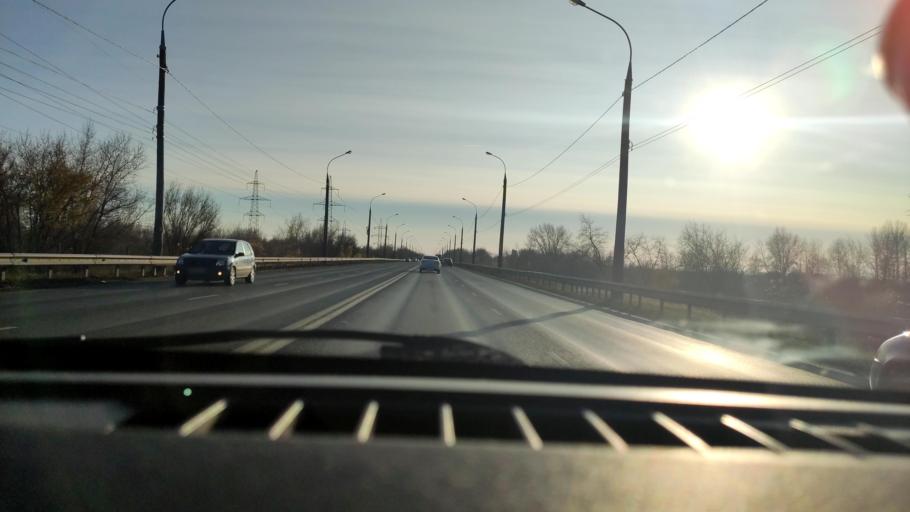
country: RU
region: Samara
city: Samara
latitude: 53.1604
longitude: 50.1936
